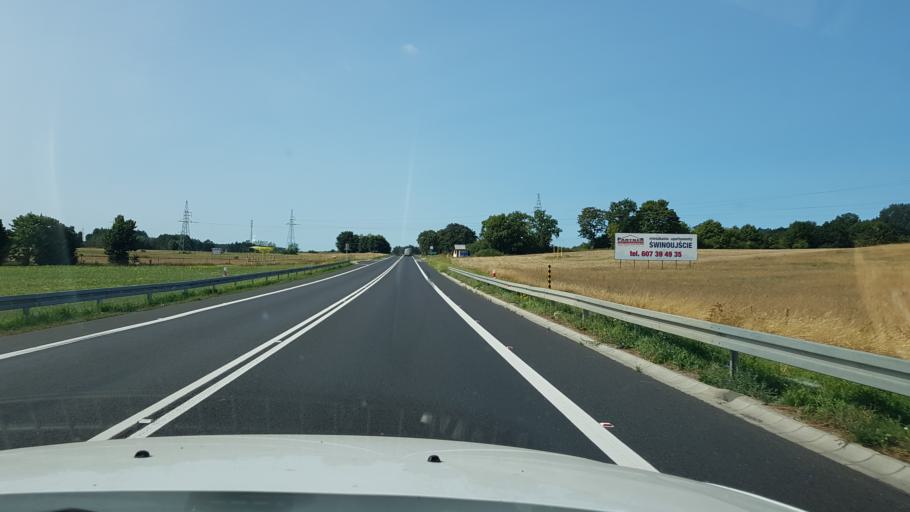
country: PL
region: West Pomeranian Voivodeship
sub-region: Powiat kamienski
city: Wolin
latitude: 53.8625
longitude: 14.5559
